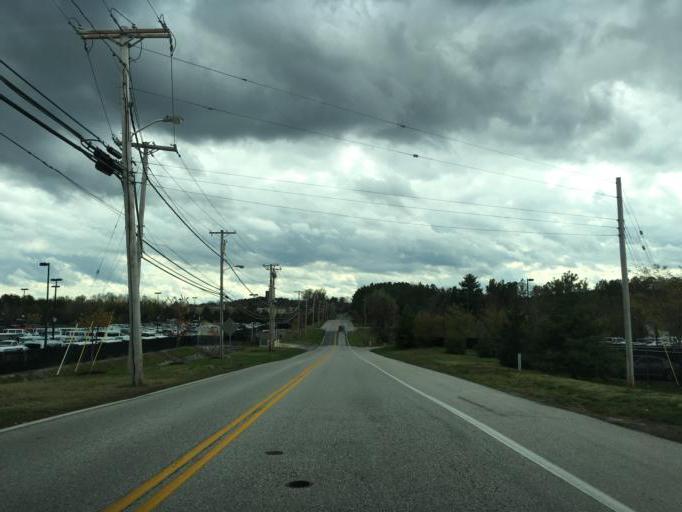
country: US
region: Maryland
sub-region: Howard County
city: Hanover
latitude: 39.1780
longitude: -76.7088
